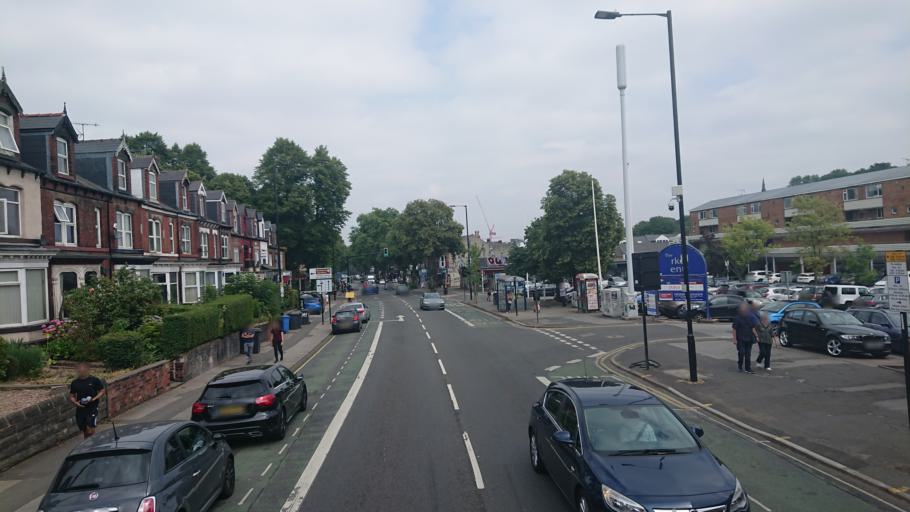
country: GB
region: England
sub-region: Sheffield
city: Sheffield
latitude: 53.3694
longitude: -1.4948
